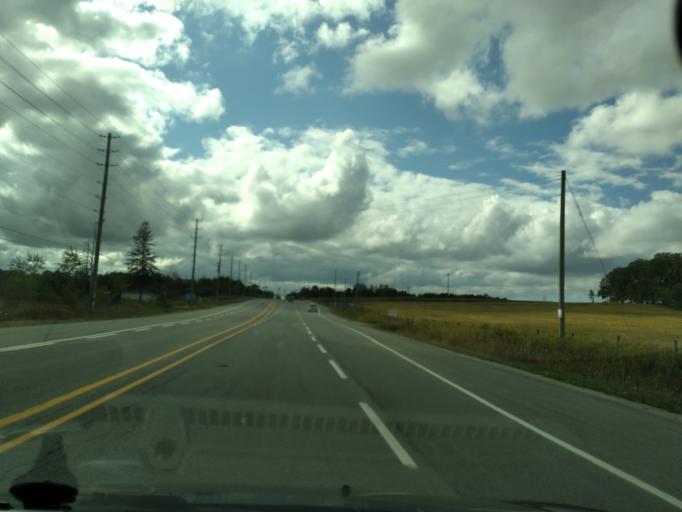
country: CA
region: Ontario
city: Innisfil
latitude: 44.2926
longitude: -79.6465
